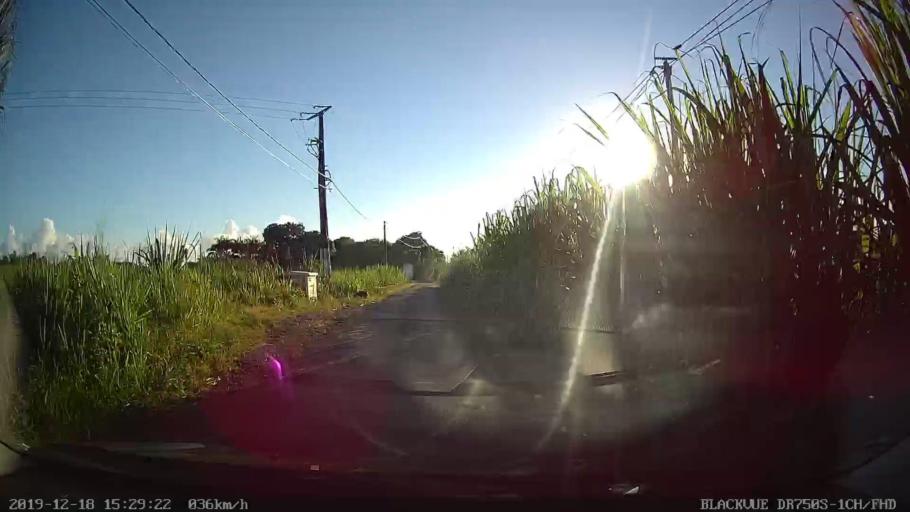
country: RE
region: Reunion
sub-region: Reunion
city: Bras-Panon
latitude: -20.9987
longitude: 55.6612
